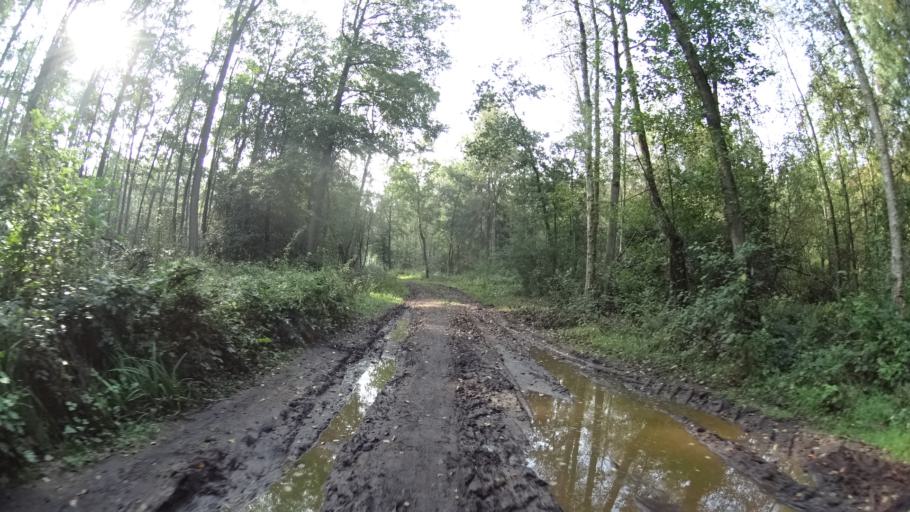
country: DE
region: Lower Saxony
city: Reppenstedt
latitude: 53.2274
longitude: 10.3444
